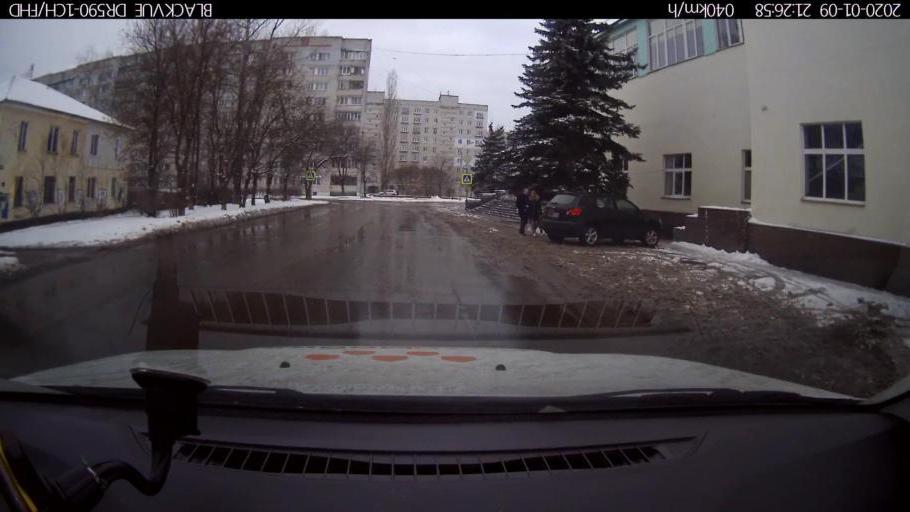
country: RU
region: Nizjnij Novgorod
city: Gorbatovka
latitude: 56.2924
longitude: 43.8470
